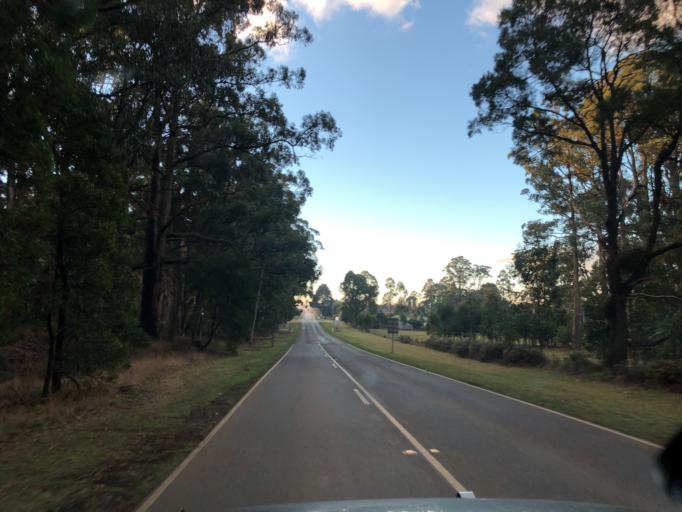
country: AU
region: Victoria
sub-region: Moorabool
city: Bacchus Marsh
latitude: -37.3996
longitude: 144.3190
